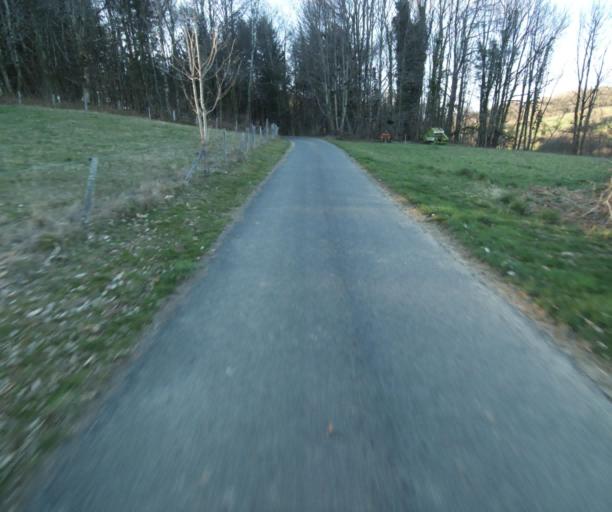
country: FR
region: Limousin
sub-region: Departement de la Correze
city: Saint-Clement
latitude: 45.3574
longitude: 1.6915
